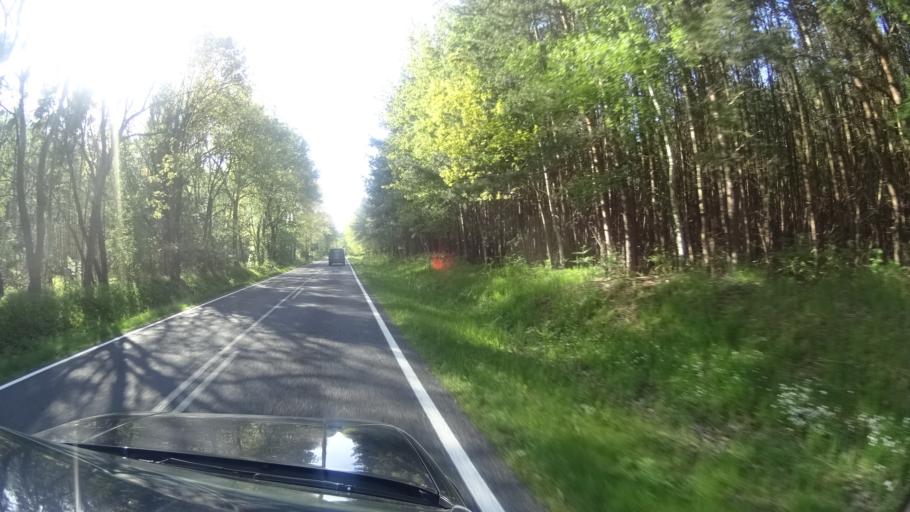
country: DE
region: Mecklenburg-Vorpommern
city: Born
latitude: 54.4001
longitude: 12.4896
